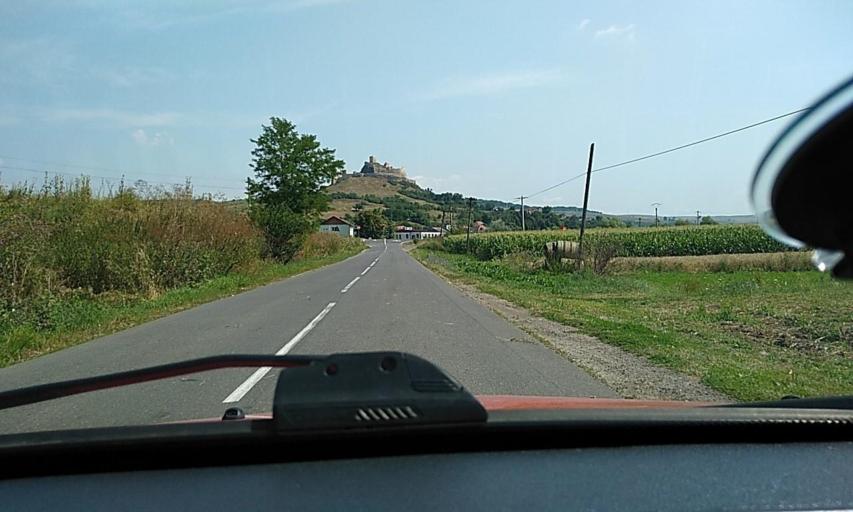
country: RO
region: Brasov
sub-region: Oras Rupea
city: Rupea
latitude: 46.0289
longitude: 25.2038
